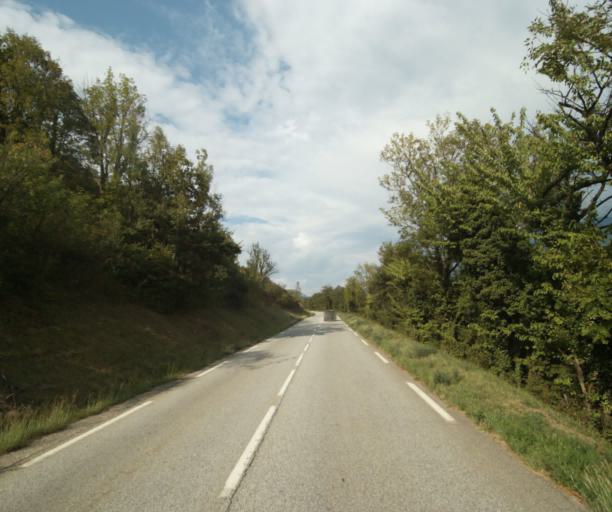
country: FR
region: Rhone-Alpes
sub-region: Departement de l'Isere
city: Brie-et-Angonnes
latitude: 45.1017
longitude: 5.7877
